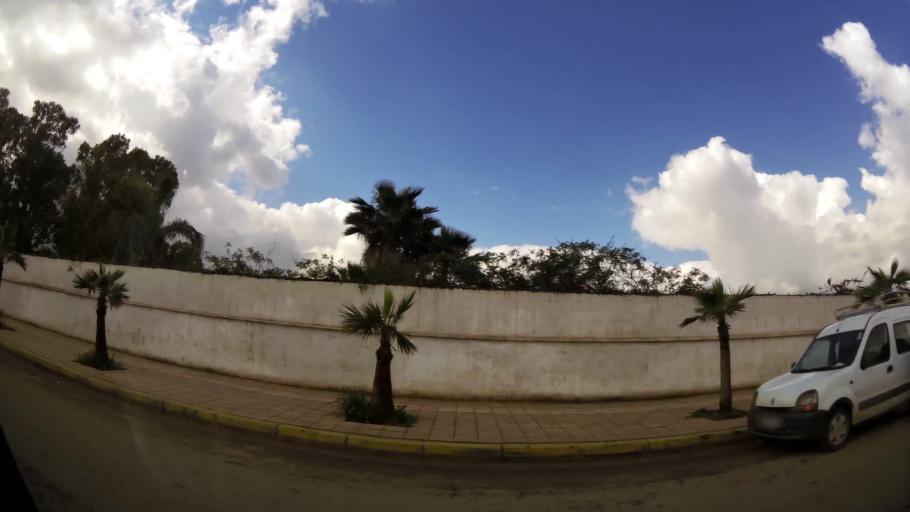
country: MA
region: Grand Casablanca
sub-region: Mediouna
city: Tit Mellil
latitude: 33.5554
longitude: -7.4821
